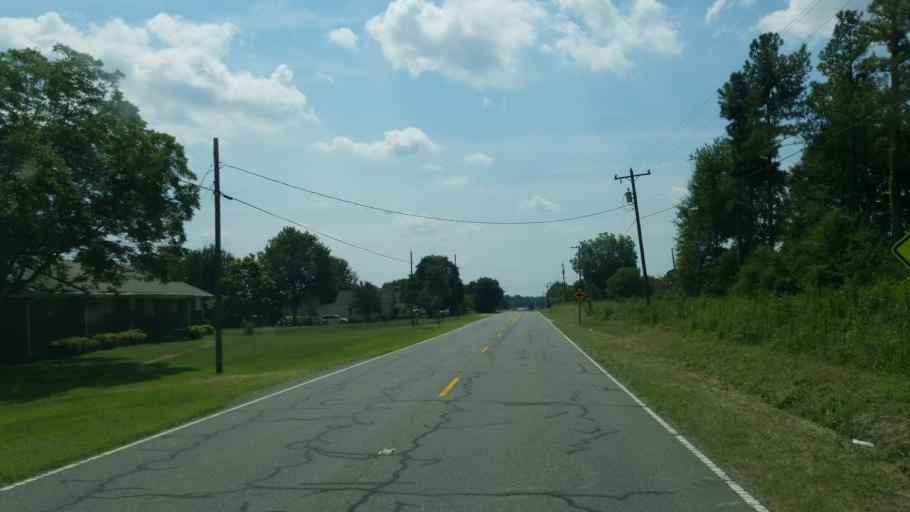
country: US
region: North Carolina
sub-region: Gaston County
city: Cherryville
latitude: 35.4385
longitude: -81.4217
